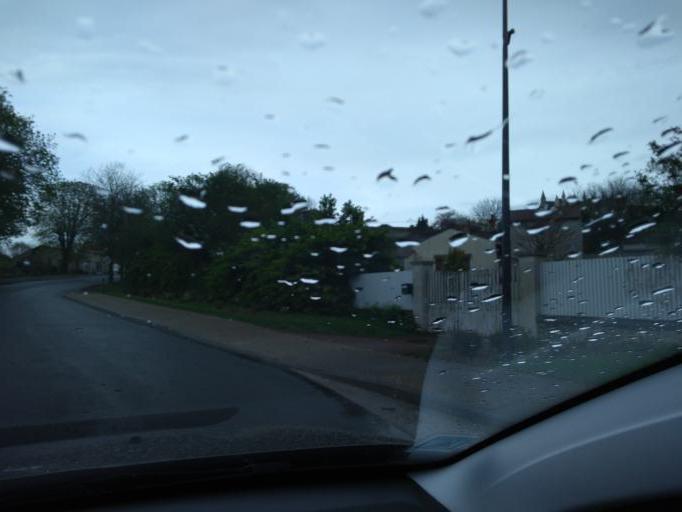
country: FR
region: Poitou-Charentes
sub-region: Departement de la Vienne
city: Loudun
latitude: 47.0093
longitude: 0.0764
